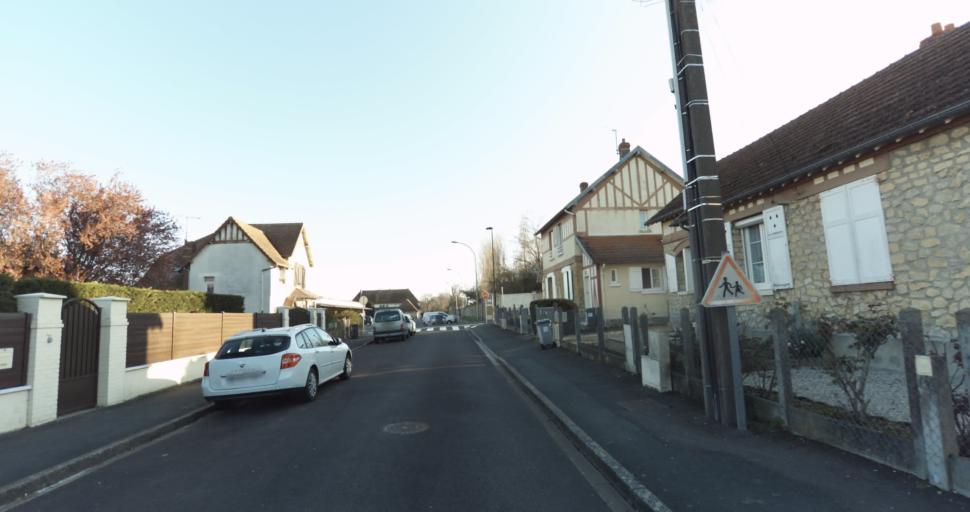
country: FR
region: Lower Normandy
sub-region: Departement du Calvados
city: Saint-Pierre-sur-Dives
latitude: 49.0155
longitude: -0.0330
